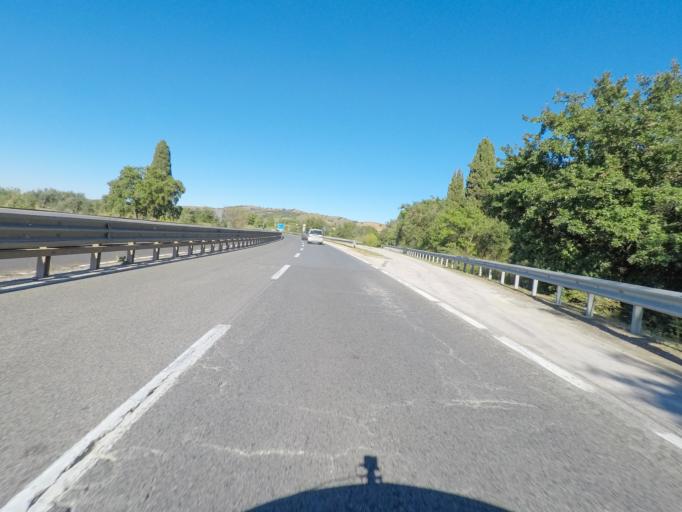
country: IT
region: Tuscany
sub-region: Provincia di Grosseto
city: Grosseto
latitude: 42.7104
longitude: 11.1437
